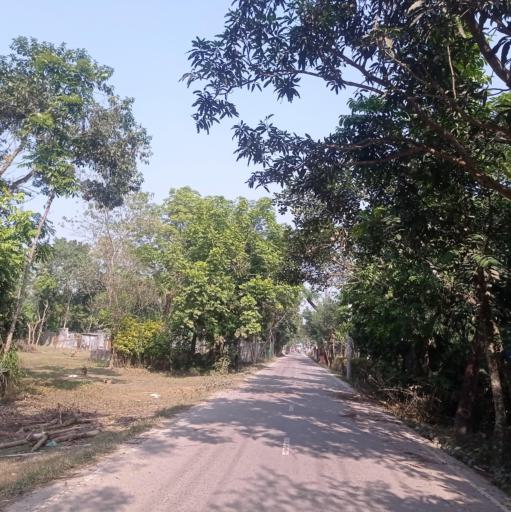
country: BD
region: Dhaka
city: Narsingdi
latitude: 24.0438
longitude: 90.6794
